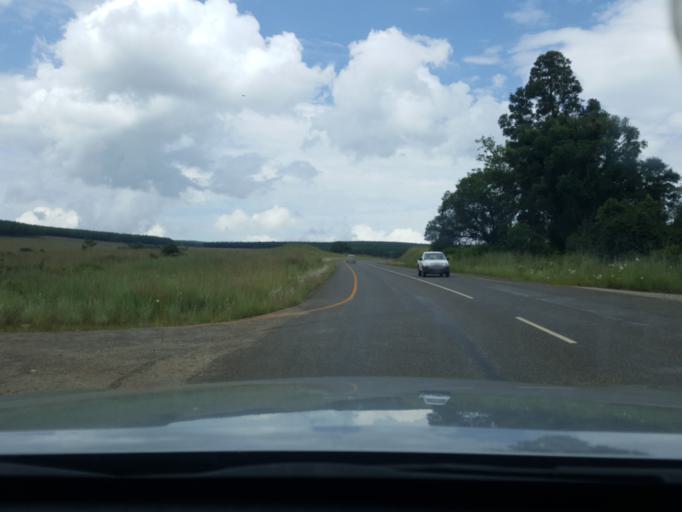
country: ZA
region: Mpumalanga
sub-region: Ehlanzeni District
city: Graksop
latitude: -25.1493
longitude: 30.8265
